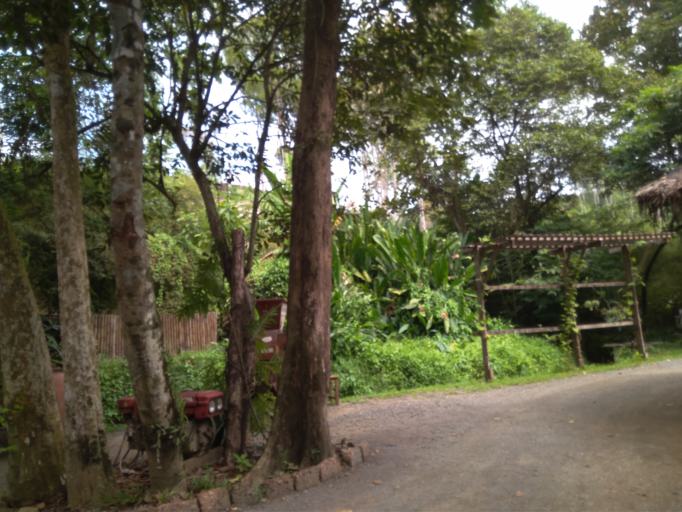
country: TH
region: Phangnga
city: Ko Yao
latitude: 8.1186
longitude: 98.6215
